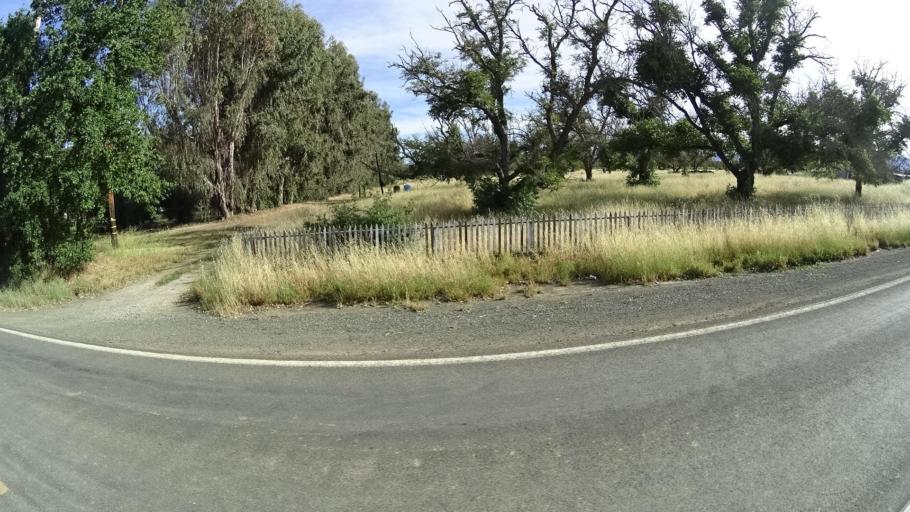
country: US
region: California
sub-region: Lake County
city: Lakeport
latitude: 39.0080
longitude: -122.8880
